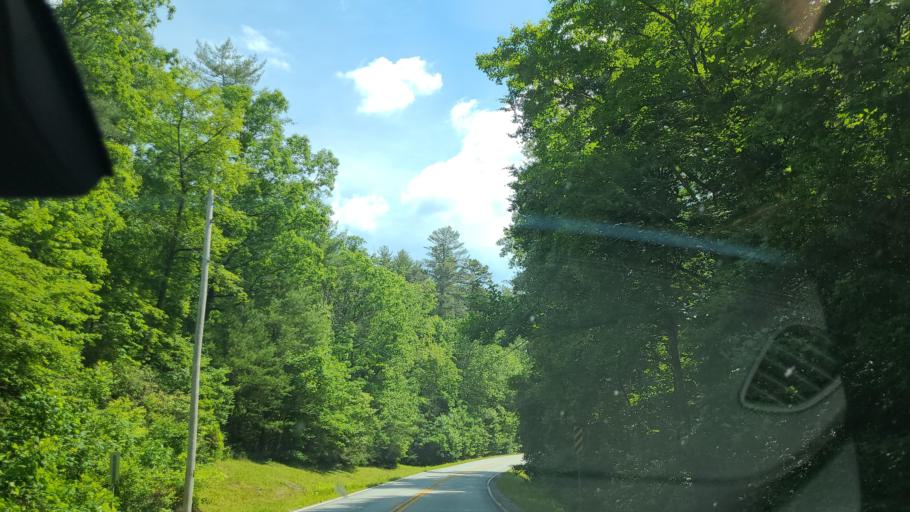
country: US
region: Georgia
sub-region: Rabun County
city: Mountain City
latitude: 34.9494
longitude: -83.1858
